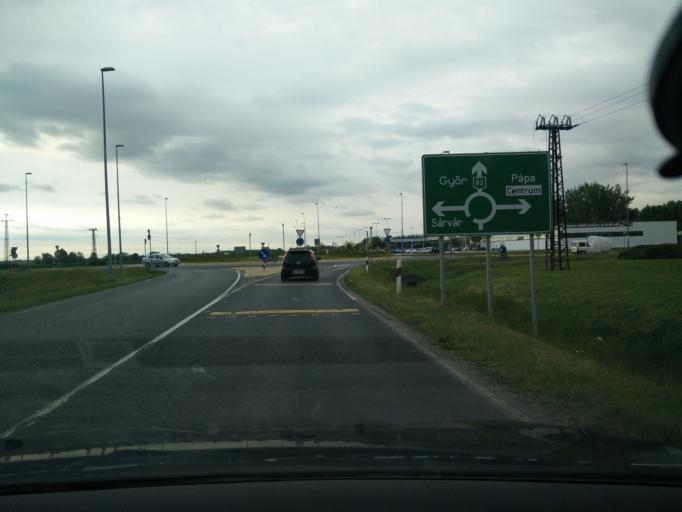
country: HU
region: Veszprem
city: Papa
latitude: 47.3210
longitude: 17.4469
